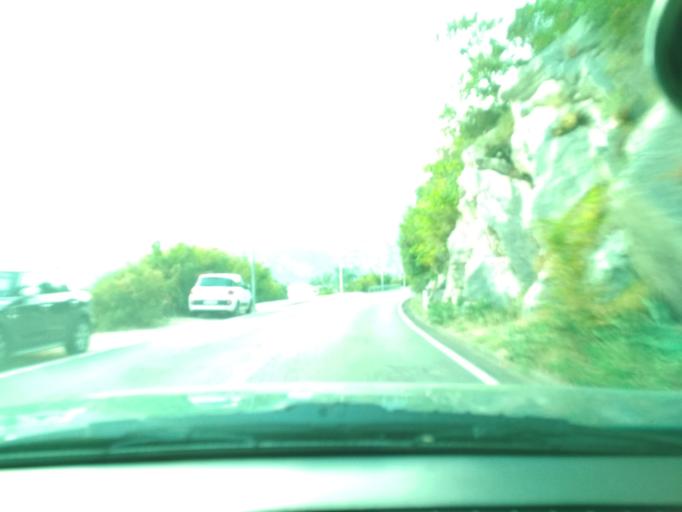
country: ME
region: Kotor
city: Risan
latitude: 42.4908
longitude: 18.6924
